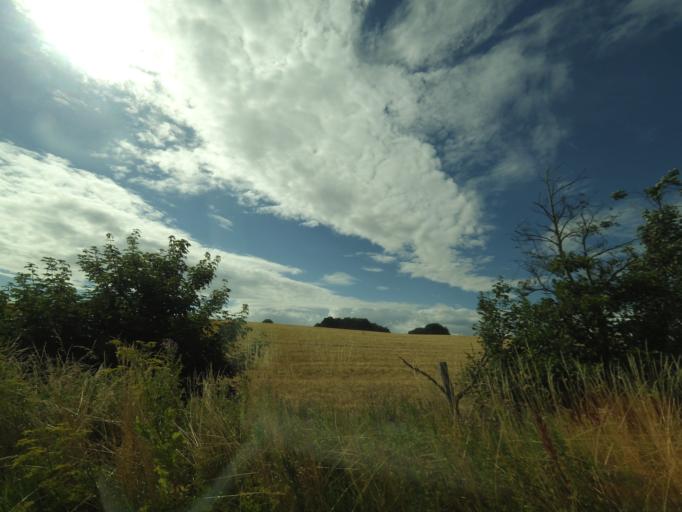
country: DK
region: South Denmark
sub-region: Assens Kommune
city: Vissenbjerg
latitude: 55.4196
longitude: 10.1773
